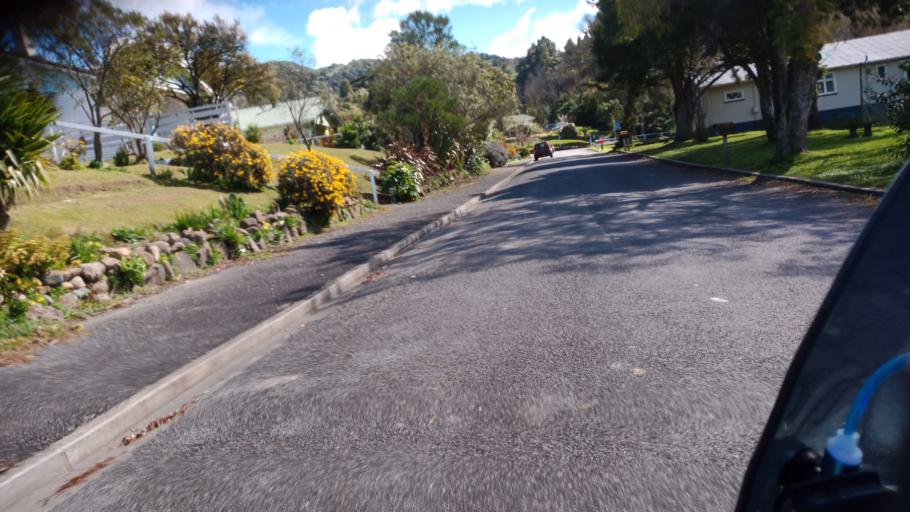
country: NZ
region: Hawke's Bay
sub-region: Wairoa District
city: Wairoa
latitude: -38.8133
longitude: 177.1480
